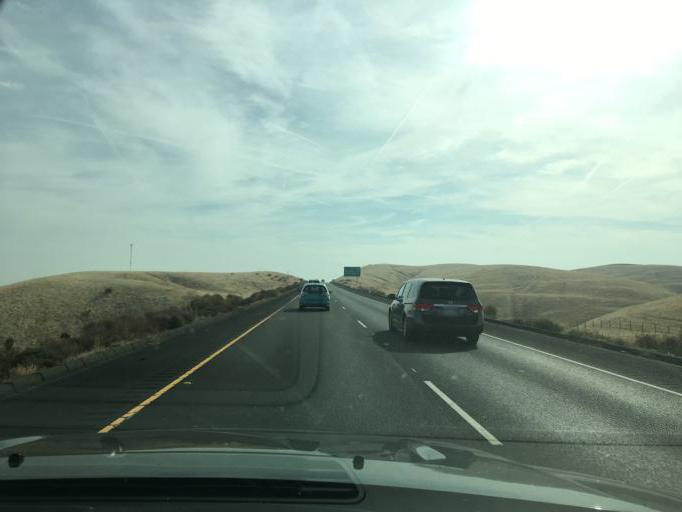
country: US
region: California
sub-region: Kings County
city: Kettleman City
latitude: 36.0009
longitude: -119.9802
